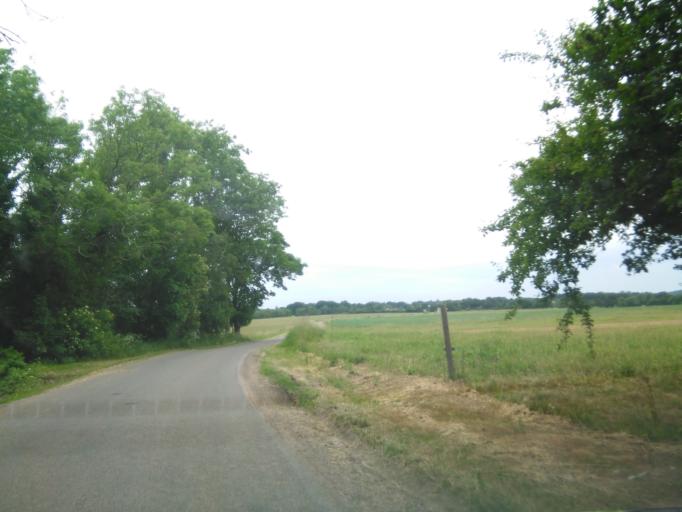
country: DK
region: Capital Region
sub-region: Bornholm Kommune
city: Akirkeby
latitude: 55.0906
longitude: 14.9130
